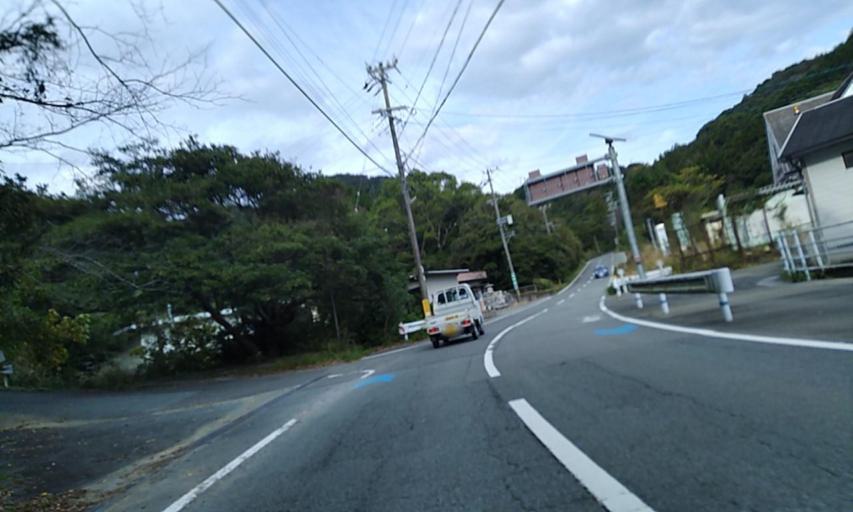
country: JP
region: Mie
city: Ise
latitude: 34.2897
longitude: 136.5708
